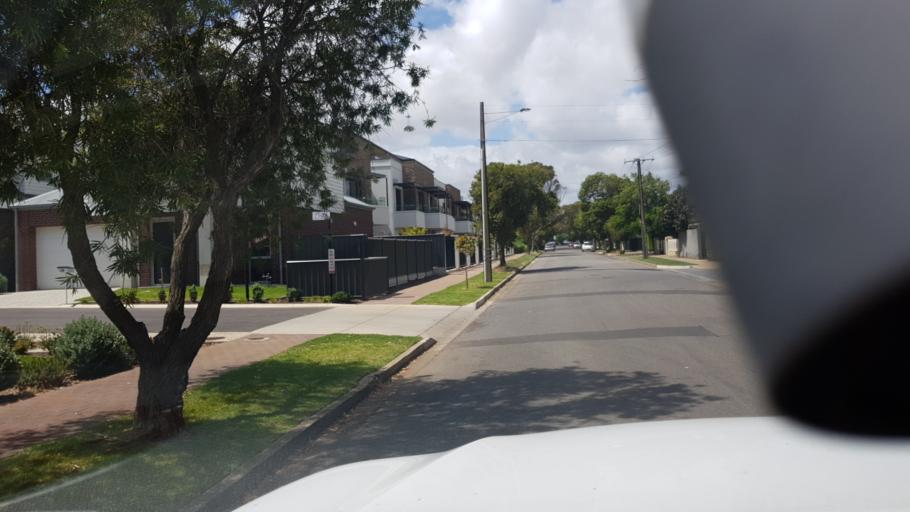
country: AU
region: South Australia
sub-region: Holdfast Bay
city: North Brighton
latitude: -34.9959
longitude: 138.5268
